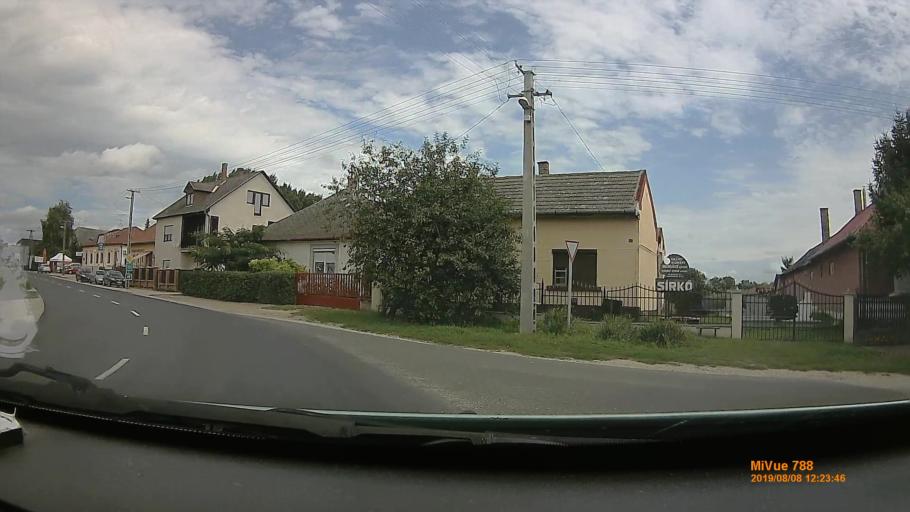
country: HU
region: Szabolcs-Szatmar-Bereg
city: Nyirbogat
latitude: 47.8020
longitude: 22.0611
